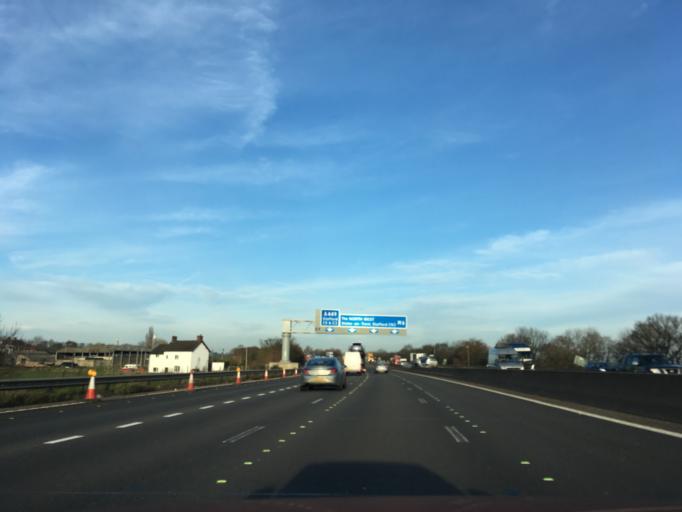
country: GB
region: England
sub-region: Staffordshire
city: Penkridge
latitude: 52.7589
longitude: -2.1029
